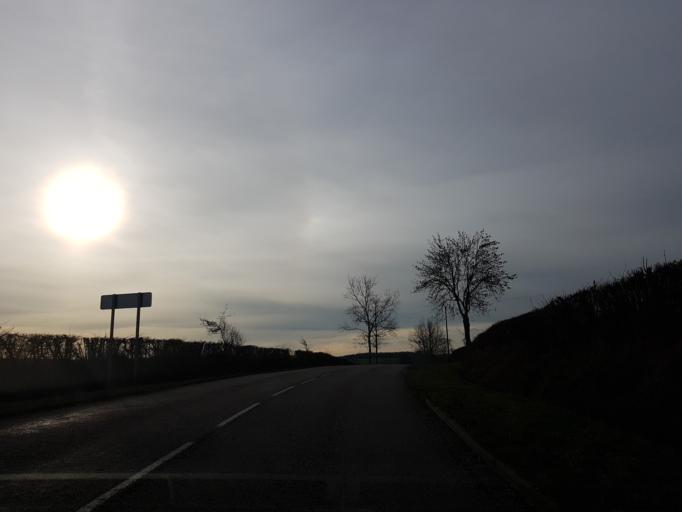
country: FR
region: Auvergne
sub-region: Departement de l'Allier
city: Souvigny
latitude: 46.4465
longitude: 3.1129
